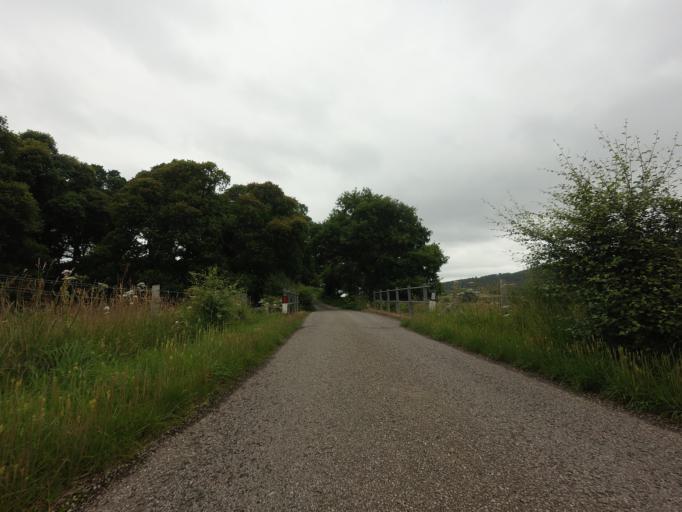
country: GB
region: Scotland
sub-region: Highland
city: Evanton
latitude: 57.9118
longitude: -4.3981
